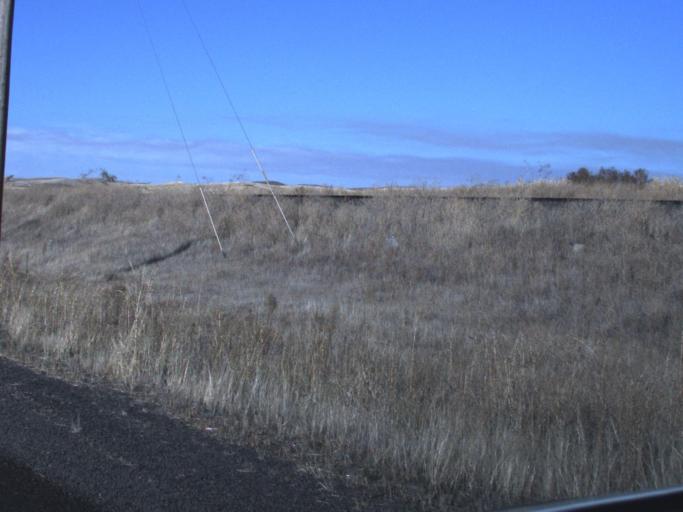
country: US
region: Washington
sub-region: Walla Walla County
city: Walla Walla
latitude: 46.1642
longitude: -118.3800
